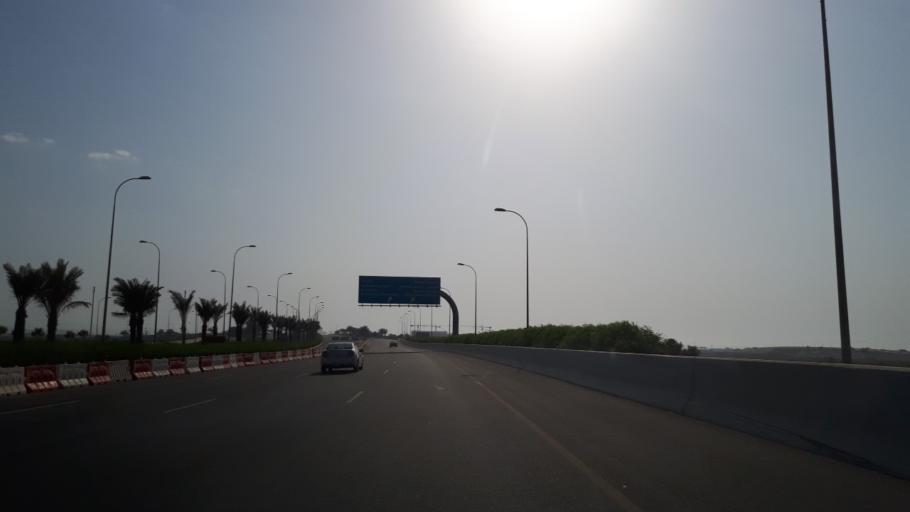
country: OM
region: Muhafazat Masqat
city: Bawshar
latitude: 23.6034
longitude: 58.3194
